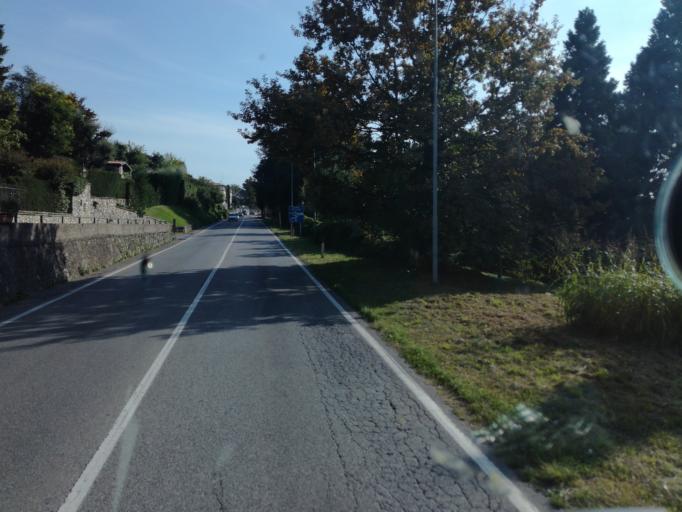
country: IT
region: Lombardy
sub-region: Provincia di Lecco
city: Vigano
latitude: 45.7212
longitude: 9.3169
